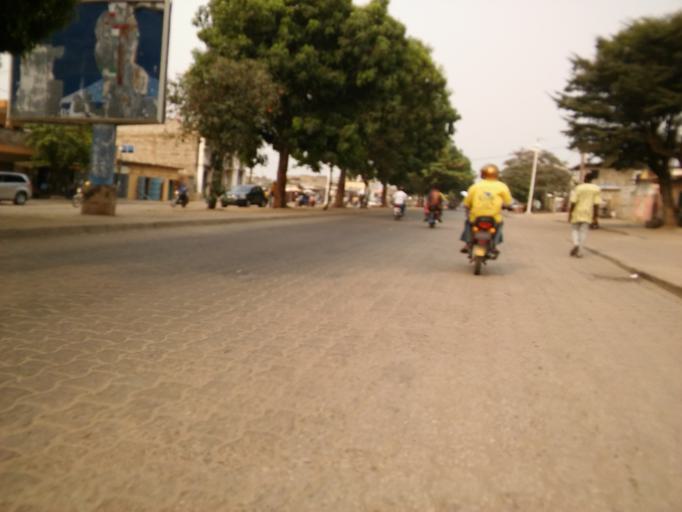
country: BJ
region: Littoral
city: Cotonou
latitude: 6.3821
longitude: 2.4136
